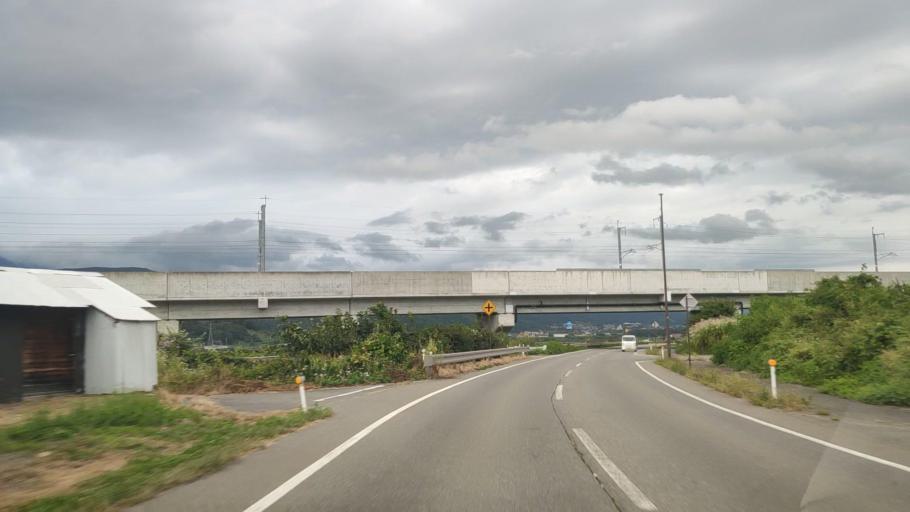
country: JP
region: Nagano
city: Nakano
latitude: 36.7892
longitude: 138.3604
